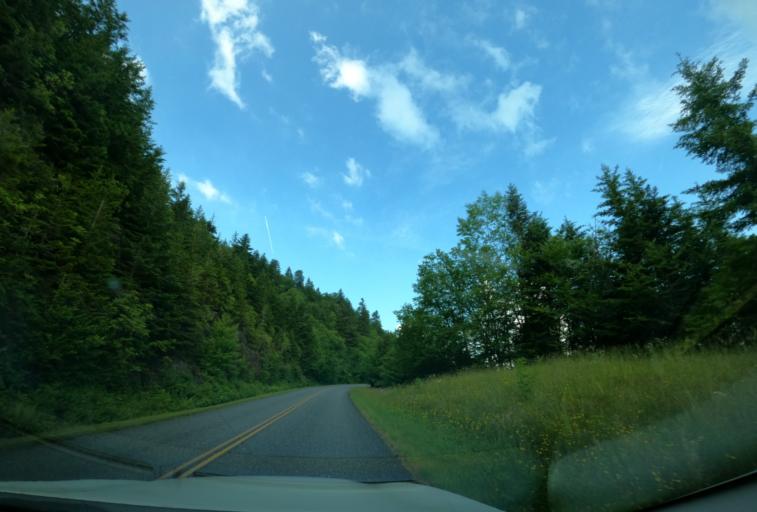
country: US
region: North Carolina
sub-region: Haywood County
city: Hazelwood
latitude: 35.3777
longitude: -83.0072
